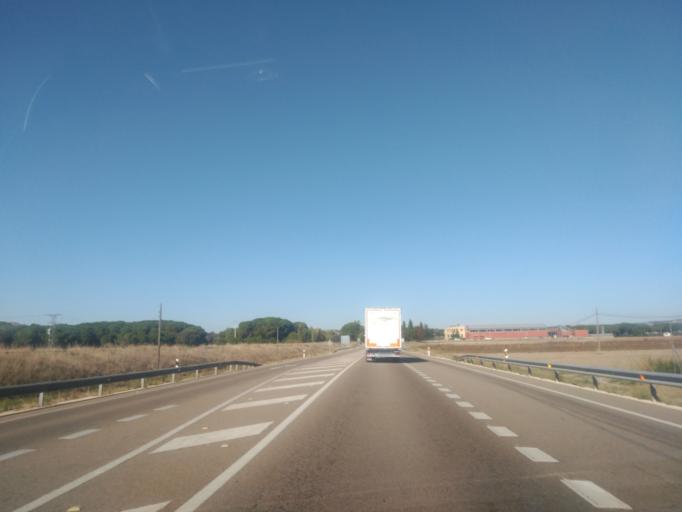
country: ES
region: Castille and Leon
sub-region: Provincia de Valladolid
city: Manzanillo
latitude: 41.6113
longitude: -4.1679
